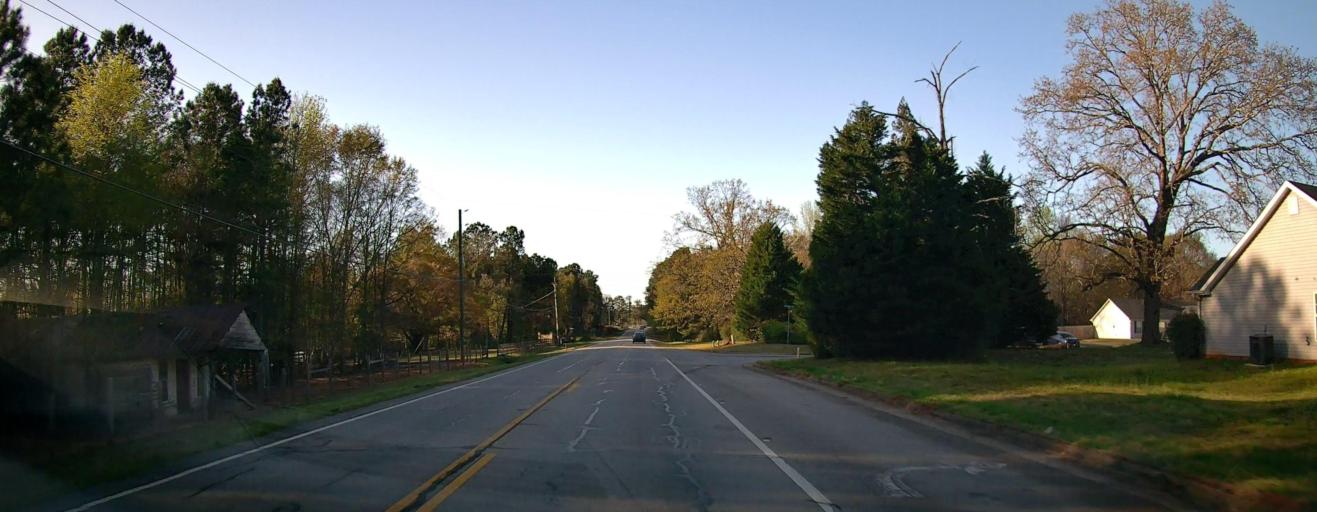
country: US
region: Georgia
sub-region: Newton County
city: Oakwood
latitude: 33.4729
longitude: -83.9124
